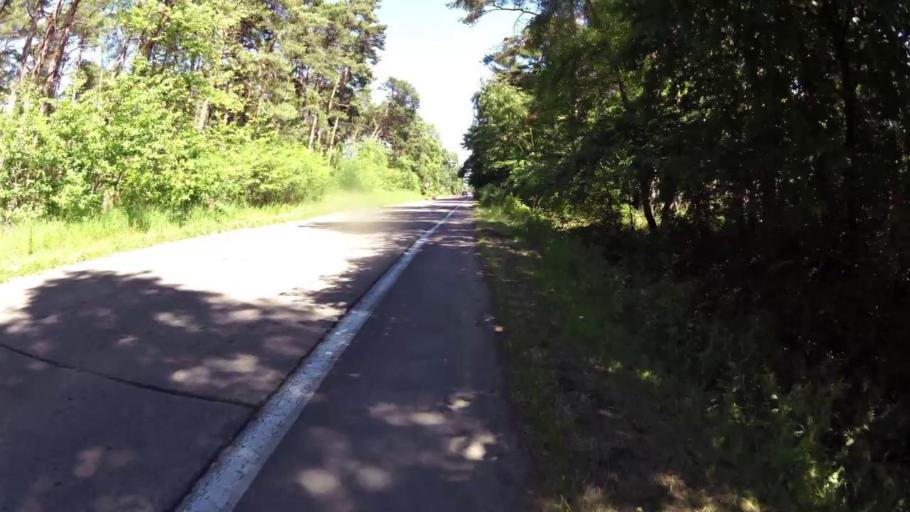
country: PL
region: West Pomeranian Voivodeship
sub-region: Powiat gryficki
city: Mrzezyno
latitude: 54.1494
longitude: 15.3271
